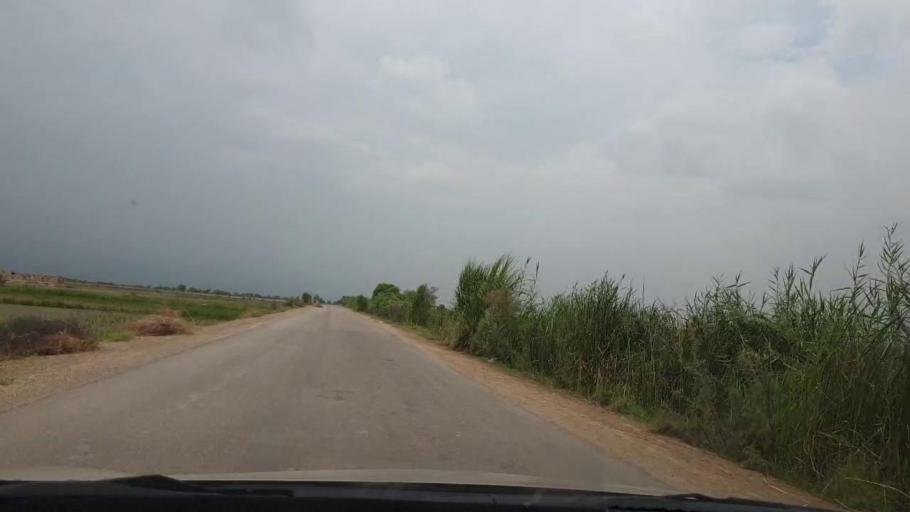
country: PK
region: Sindh
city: Ratodero
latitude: 27.8050
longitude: 68.3098
